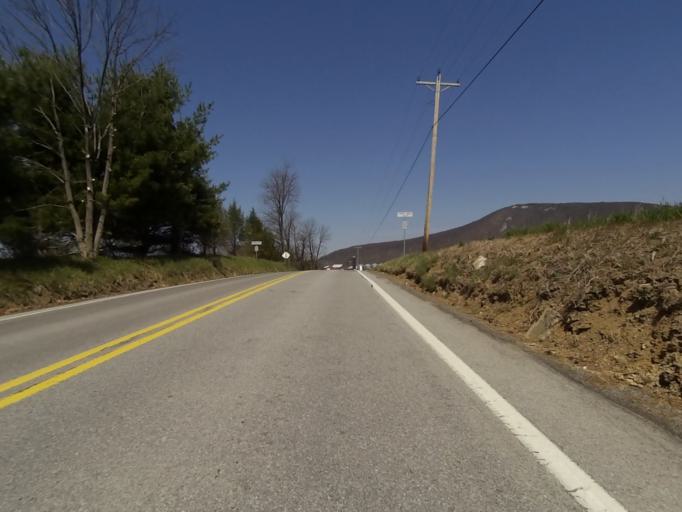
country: US
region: Pennsylvania
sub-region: Blair County
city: Tyrone
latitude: 40.5918
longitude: -78.1373
